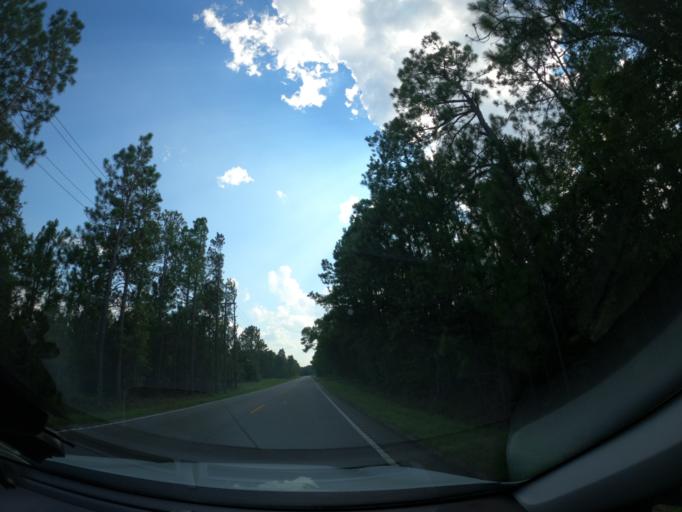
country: US
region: South Carolina
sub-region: Barnwell County
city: Williston
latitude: 33.5031
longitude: -81.5092
